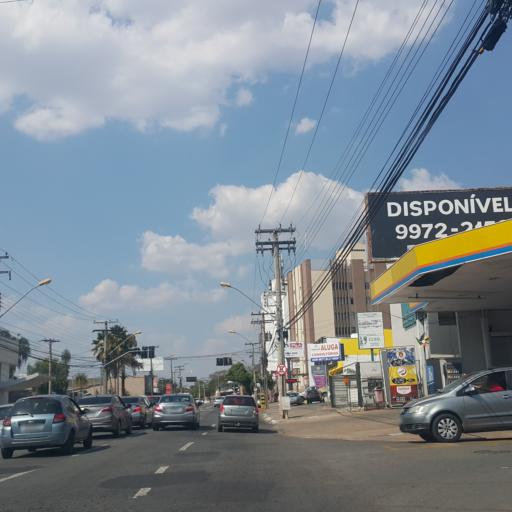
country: BR
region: Goias
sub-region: Goiania
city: Goiania
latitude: -16.6907
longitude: -49.2577
